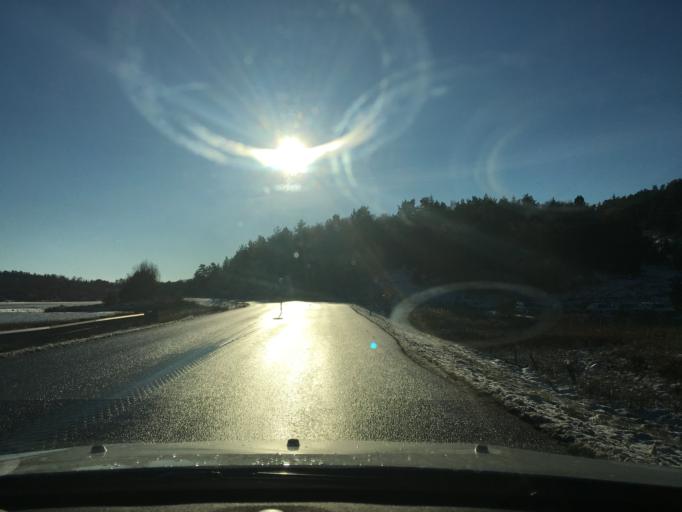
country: SE
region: Vaestra Goetaland
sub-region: Tjorns Kommun
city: Myggenas
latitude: 58.0763
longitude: 11.6962
